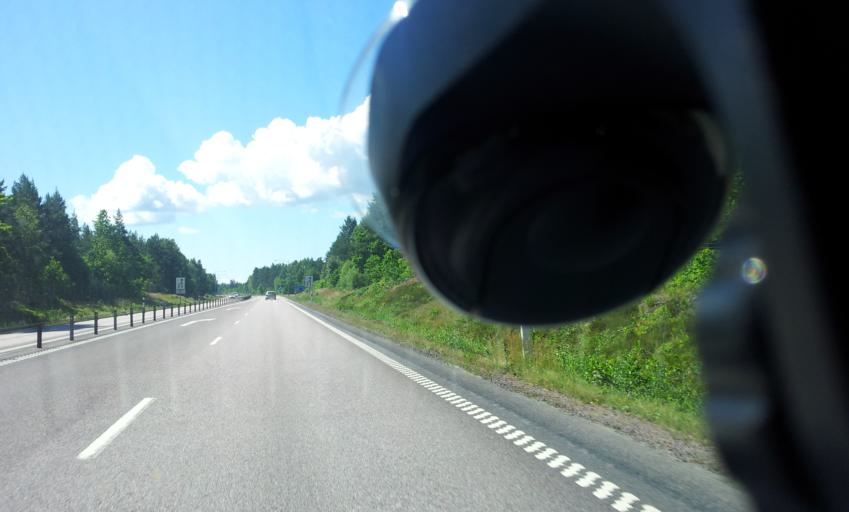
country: SE
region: Kalmar
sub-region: Oskarshamns Kommun
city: Paskallavik
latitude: 57.2002
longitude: 16.4384
